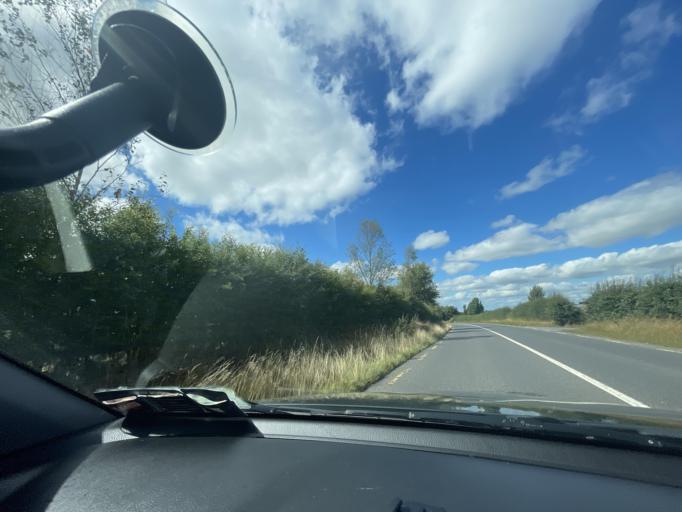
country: IE
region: Leinster
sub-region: An Mhi
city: Dunshaughlin
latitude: 53.5172
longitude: -6.6332
